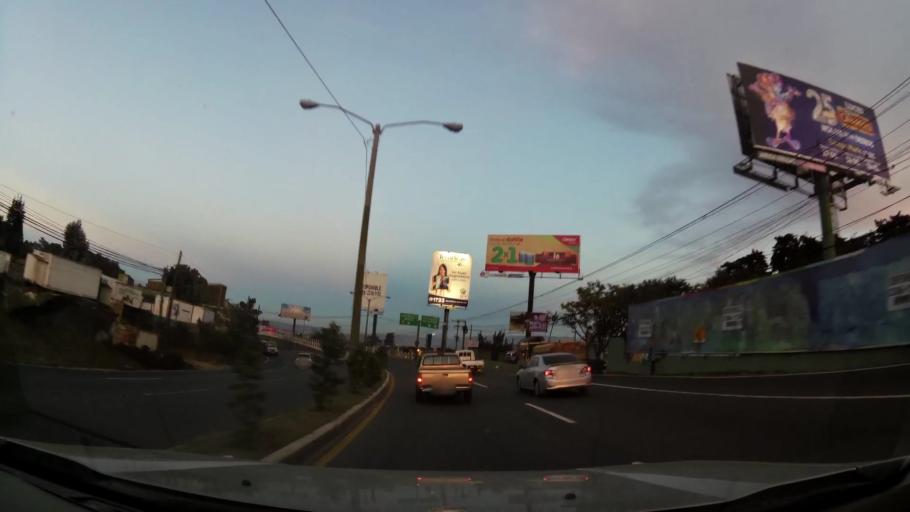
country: GT
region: Guatemala
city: Mixco
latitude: 14.6163
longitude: -90.6084
